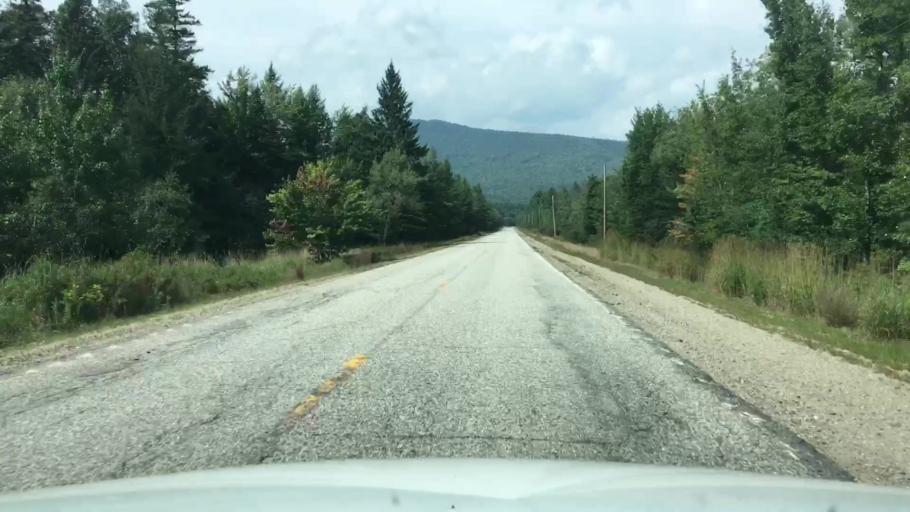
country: US
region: Maine
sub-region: Oxford County
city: Rumford
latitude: 44.5735
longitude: -70.7238
